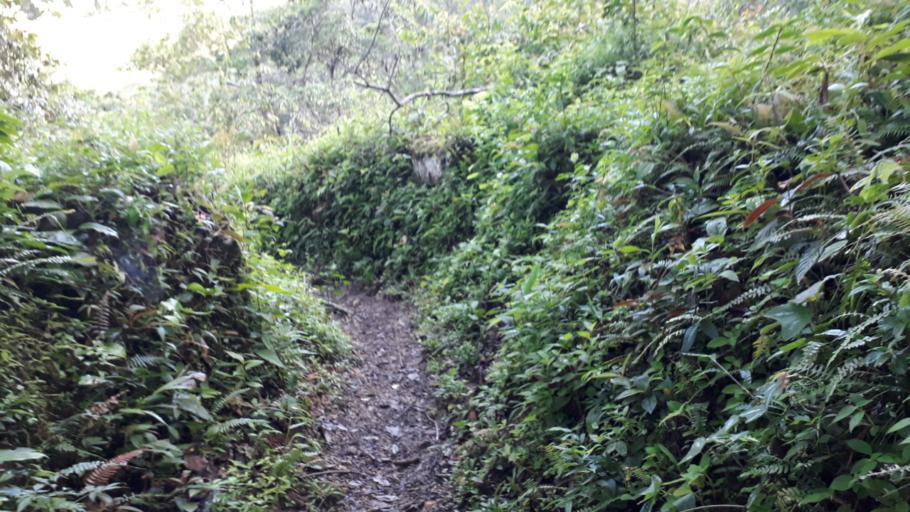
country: CO
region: Casanare
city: Nunchia
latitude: 5.6409
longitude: -72.4249
